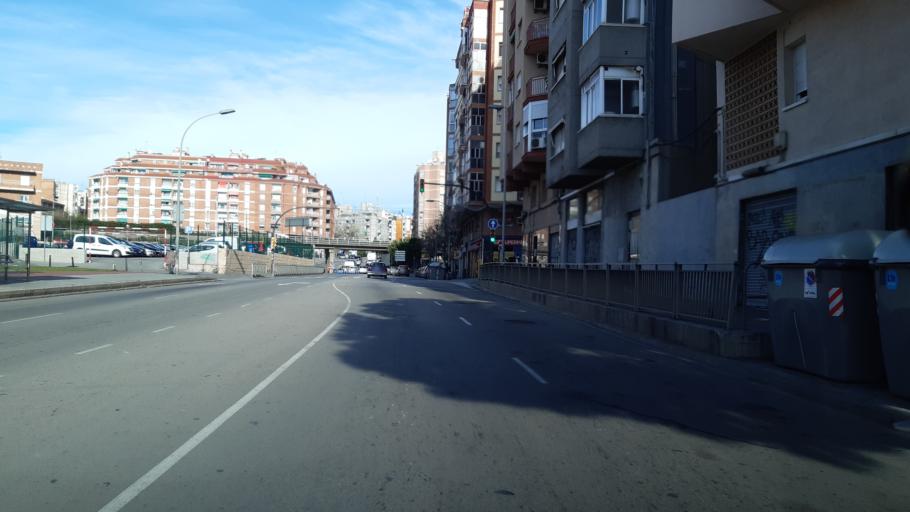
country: ES
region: Catalonia
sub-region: Provincia de Barcelona
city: L'Hospitalet de Llobregat
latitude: 41.3667
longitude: 2.1168
